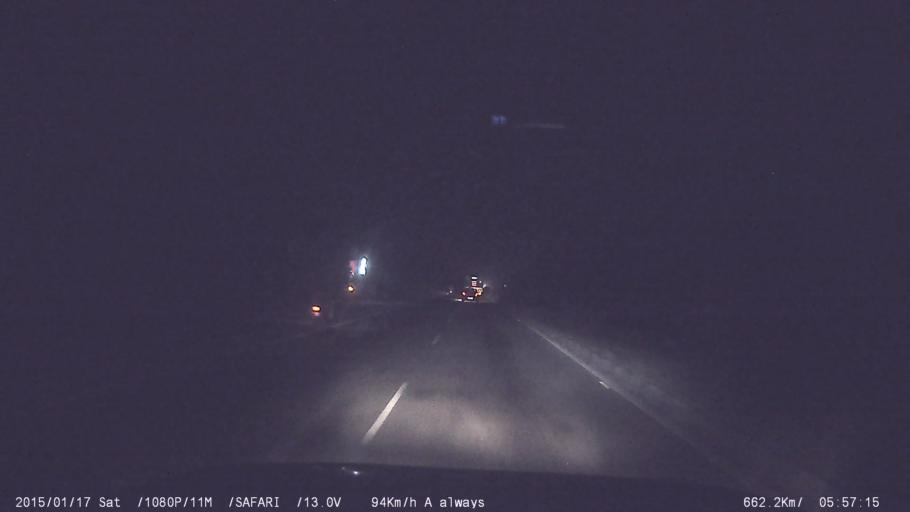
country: IN
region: Tamil Nadu
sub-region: Vellore
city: Walajapet
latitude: 12.8982
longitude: 79.5379
